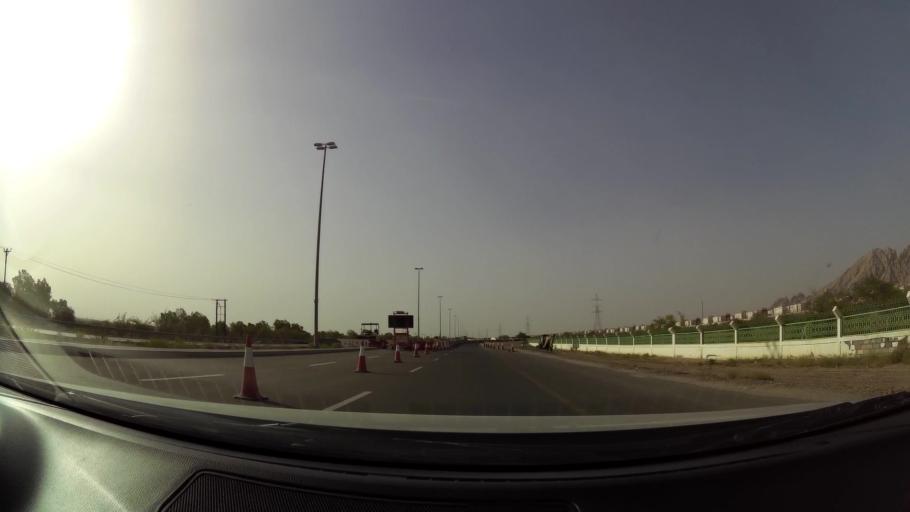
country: AE
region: Abu Dhabi
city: Al Ain
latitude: 24.0758
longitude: 55.7276
